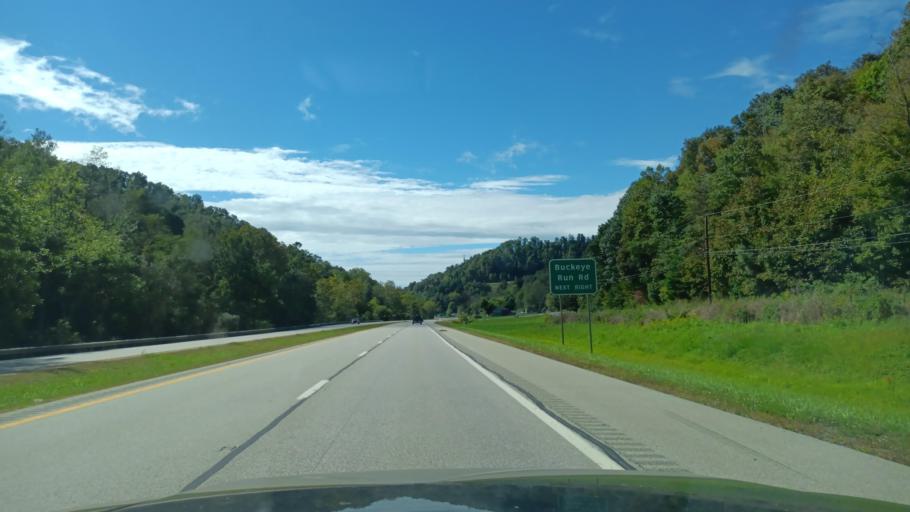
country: US
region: West Virginia
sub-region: Harrison County
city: Salem
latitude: 39.2954
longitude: -80.6254
